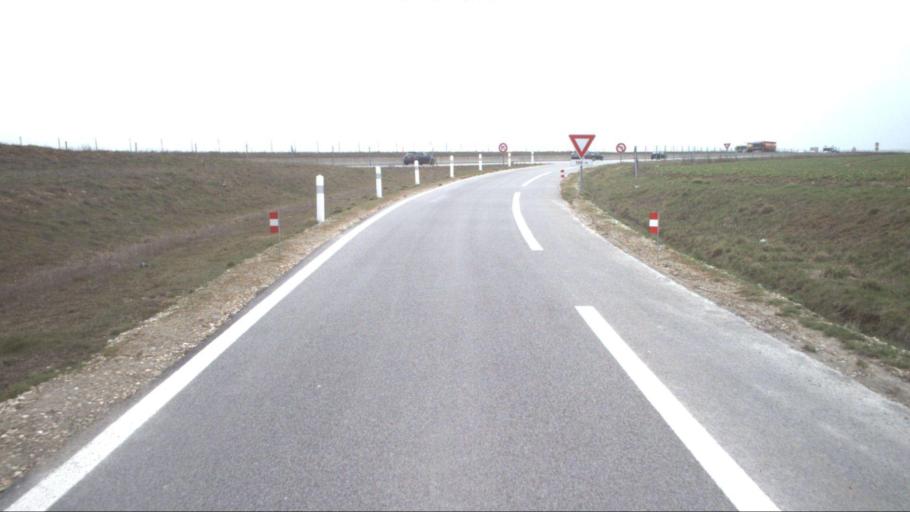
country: FR
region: Ile-de-France
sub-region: Departement des Yvelines
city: Sonchamp
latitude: 48.5784
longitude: 1.8316
